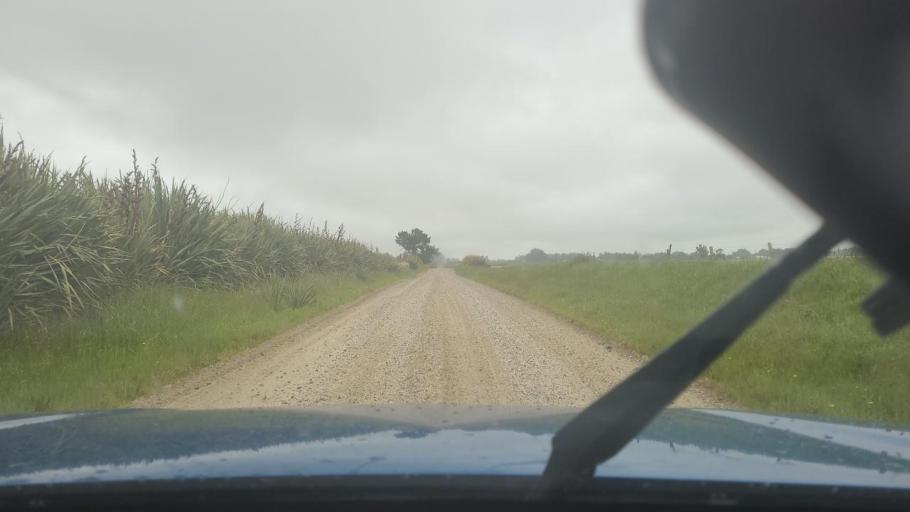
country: NZ
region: Southland
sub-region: Invercargill City
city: Invercargill
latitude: -46.3291
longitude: 168.6594
